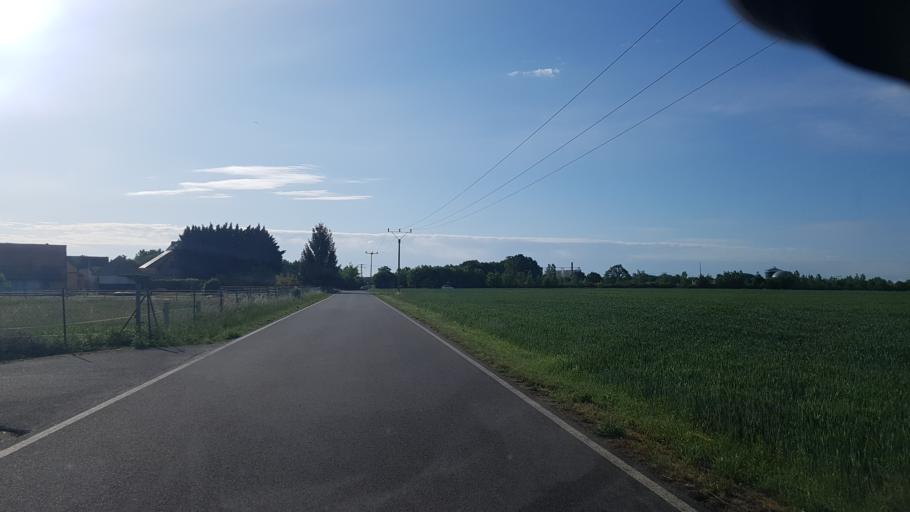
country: DE
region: Brandenburg
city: Luckau
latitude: 51.8254
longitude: 13.7577
